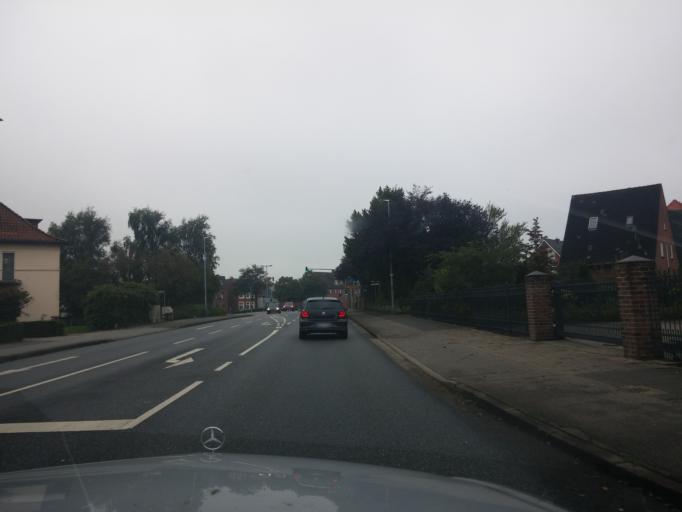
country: DE
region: Schleswig-Holstein
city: Husum
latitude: 54.4809
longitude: 9.0675
